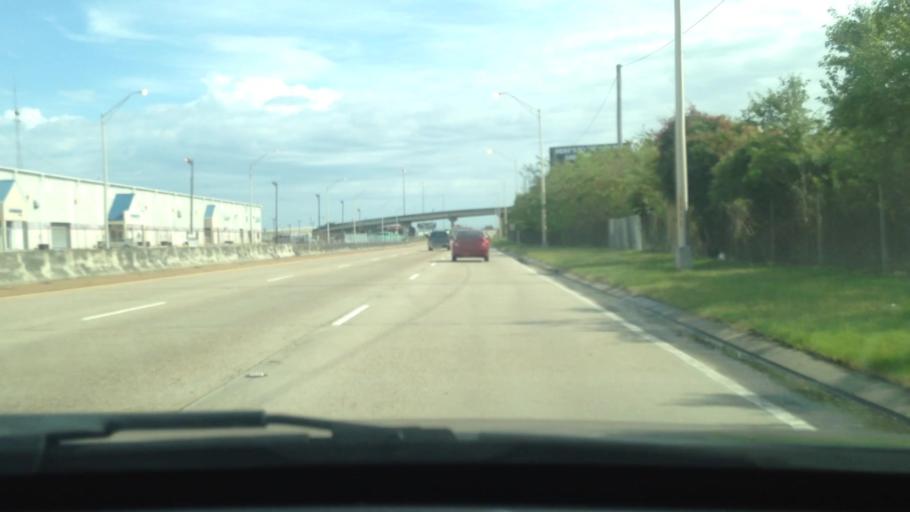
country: US
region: Louisiana
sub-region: Jefferson Parish
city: Jefferson
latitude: 29.9700
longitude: -90.1491
